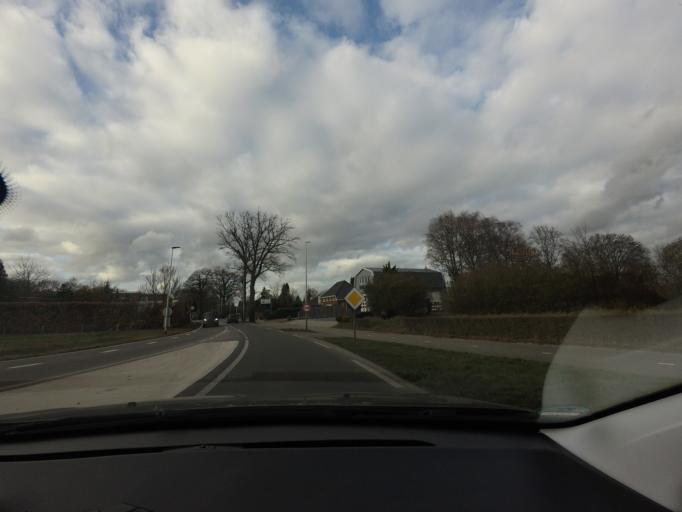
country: NL
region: Gelderland
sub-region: Gemeente Lochem
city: Eefde
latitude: 52.1769
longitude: 6.2203
